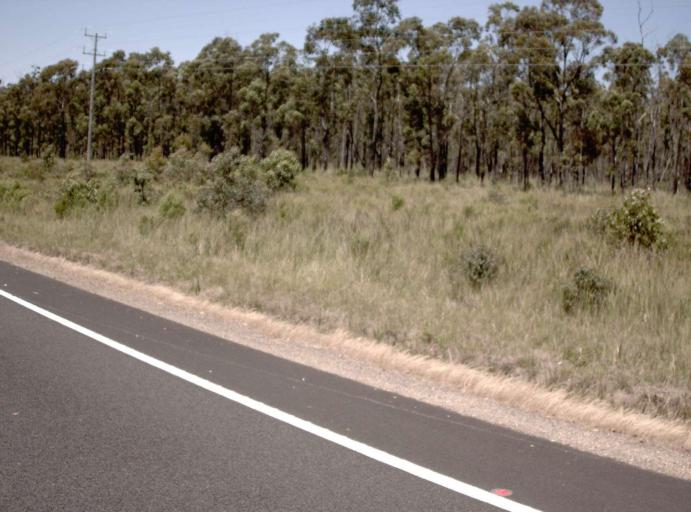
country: AU
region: Victoria
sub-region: East Gippsland
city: Lakes Entrance
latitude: -37.7553
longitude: 148.3093
